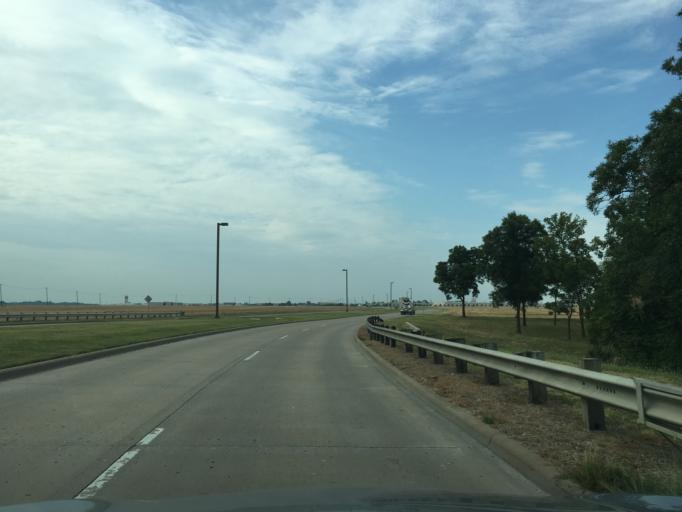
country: US
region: Texas
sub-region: Collin County
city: McKinney
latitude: 33.1942
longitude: -96.5968
